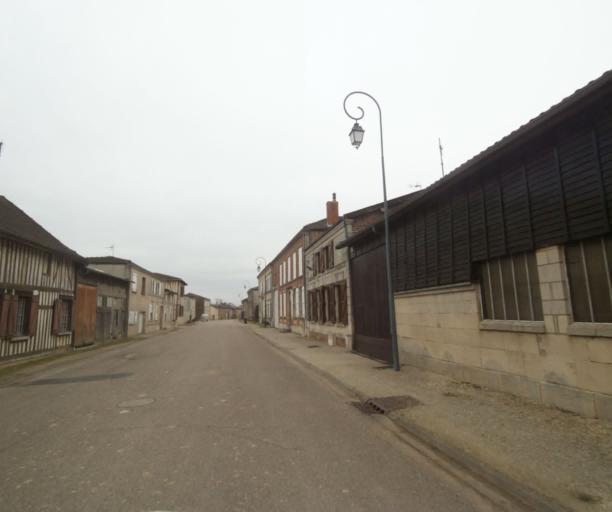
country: FR
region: Champagne-Ardenne
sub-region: Departement de la Haute-Marne
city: Villiers-en-Lieu
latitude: 48.6378
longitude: 4.7706
